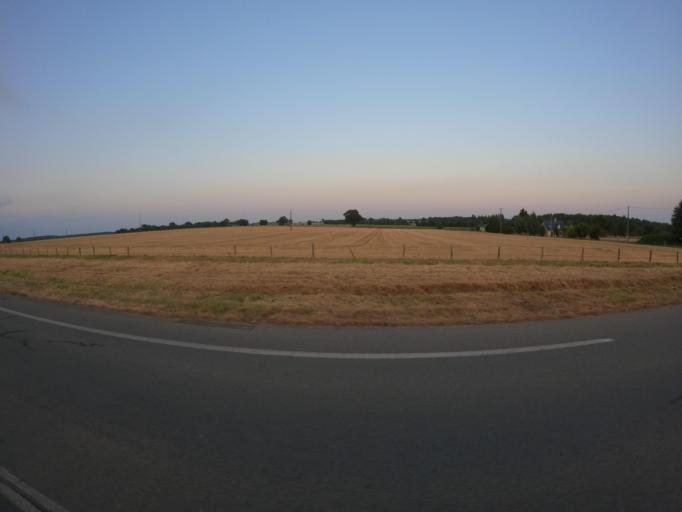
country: FR
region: Pays de la Loire
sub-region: Departement de la Mayenne
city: Chemaze
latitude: 47.7765
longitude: -0.7791
